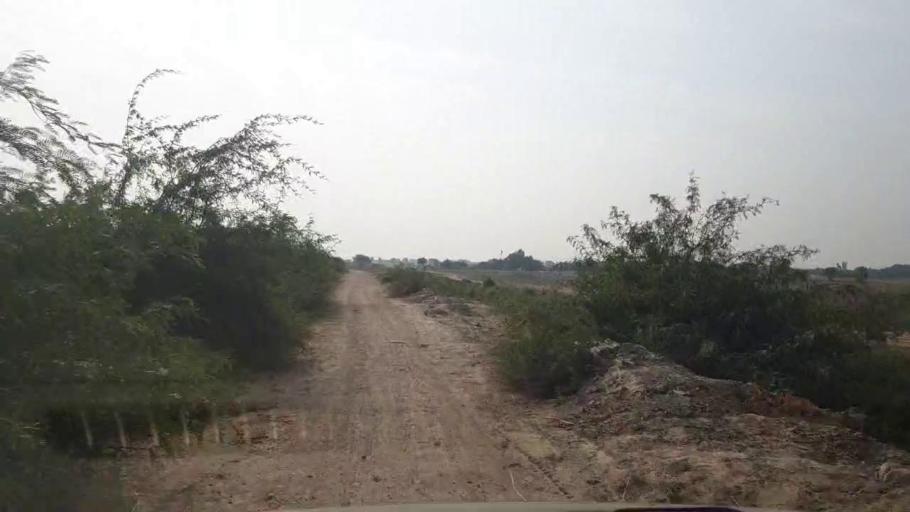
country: PK
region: Sindh
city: Tando Muhammad Khan
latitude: 25.1218
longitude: 68.4924
